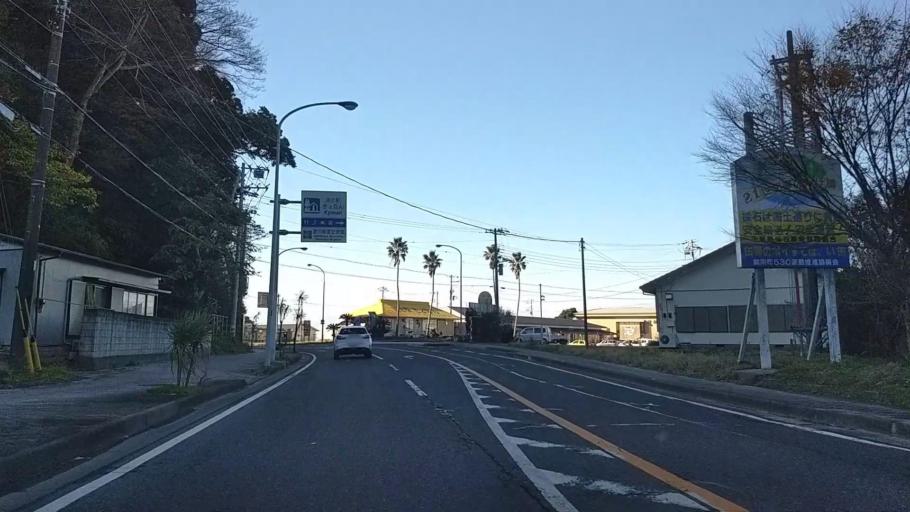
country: JP
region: Chiba
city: Tateyama
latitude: 35.1283
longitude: 139.8381
